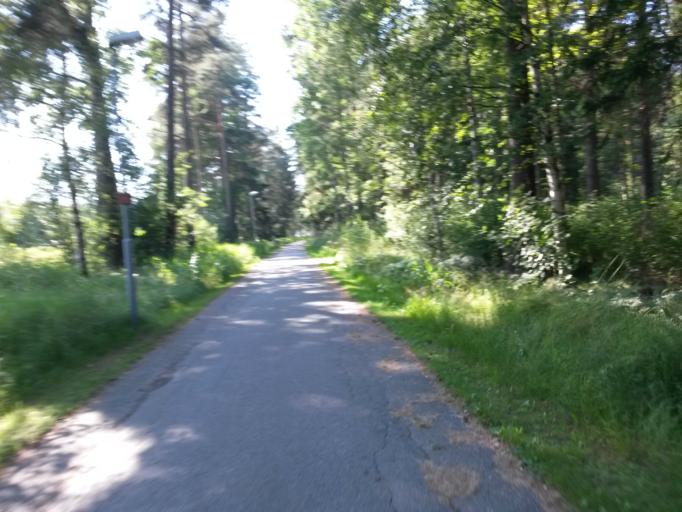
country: SE
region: Vaestra Goetaland
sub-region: Lidkopings Kommun
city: Lidkoping
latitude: 58.4936
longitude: 13.2184
